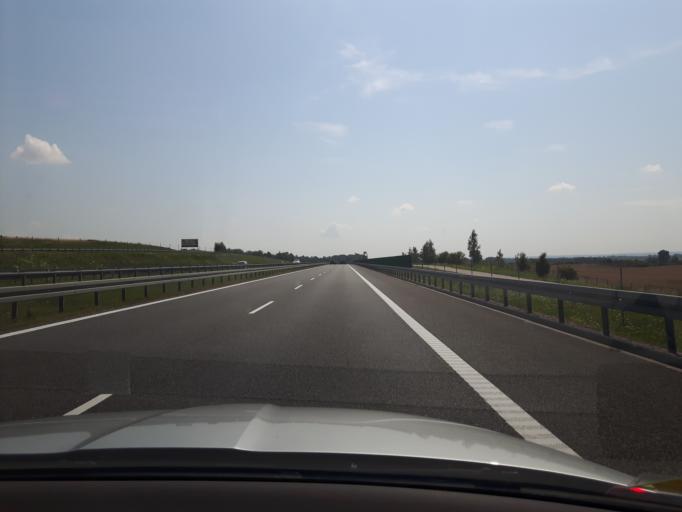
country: PL
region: Warmian-Masurian Voivodeship
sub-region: Powiat elblaski
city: Gronowo Gorne
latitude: 54.1193
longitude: 19.4719
